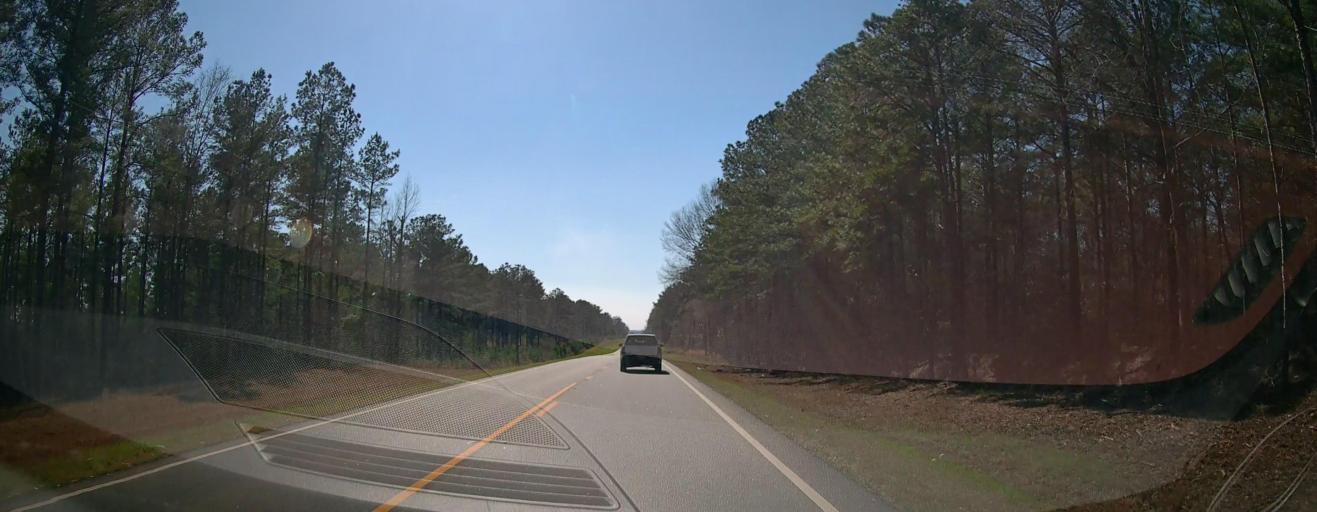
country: US
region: Georgia
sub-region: Dooly County
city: Unadilla
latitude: 32.3364
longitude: -83.8553
